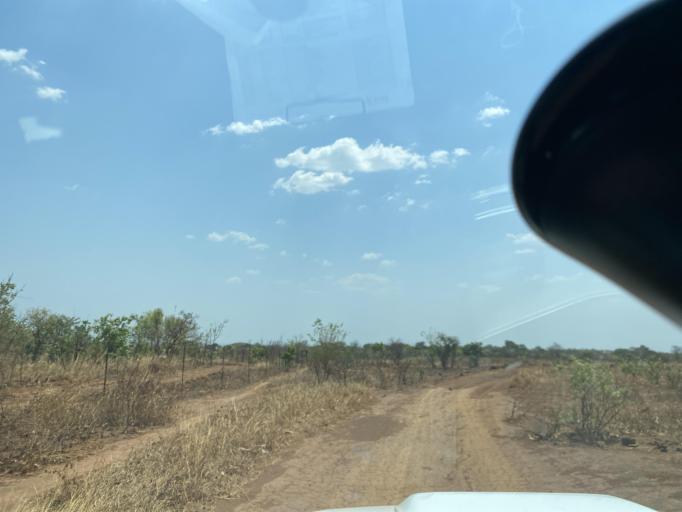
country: ZM
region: Lusaka
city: Lusaka
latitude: -15.4981
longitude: 27.9579
